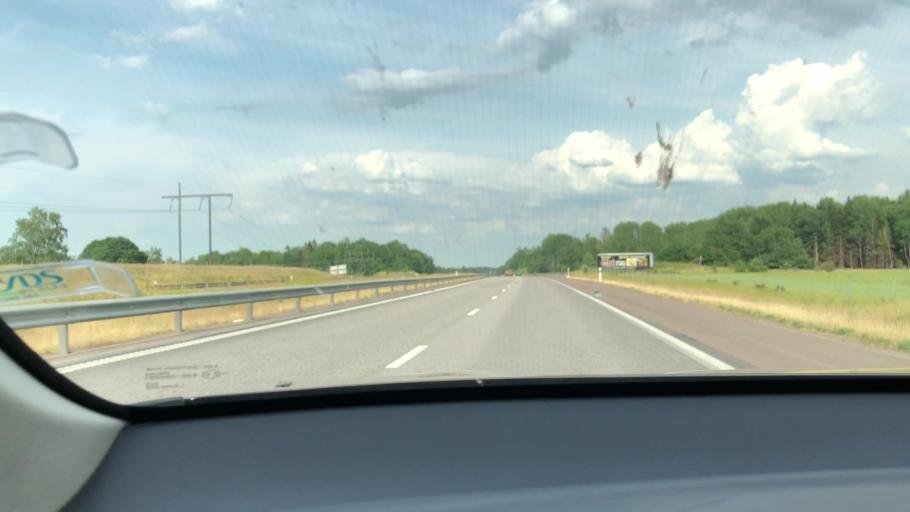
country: SE
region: OEstergoetland
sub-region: Boxholms Kommun
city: Boxholm
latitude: 58.3018
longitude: 14.9572
